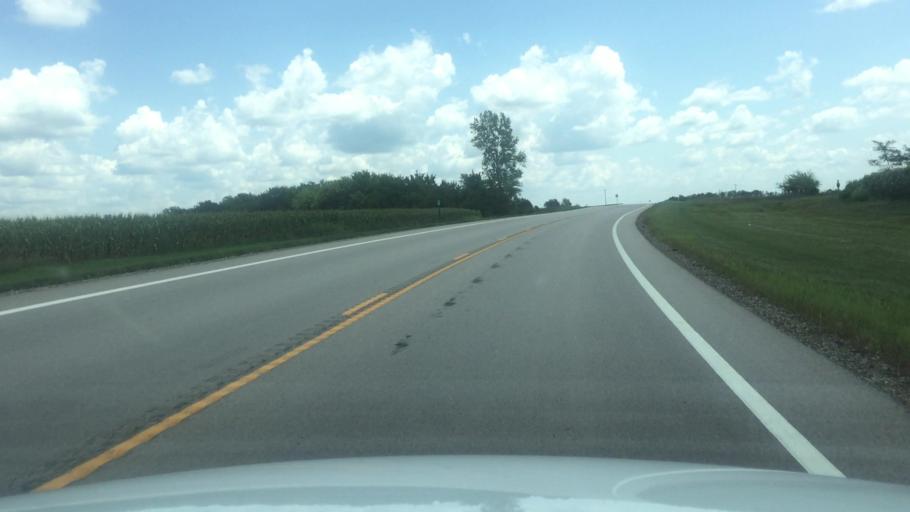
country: US
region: Kansas
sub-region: Brown County
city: Horton
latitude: 39.6665
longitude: -95.4196
